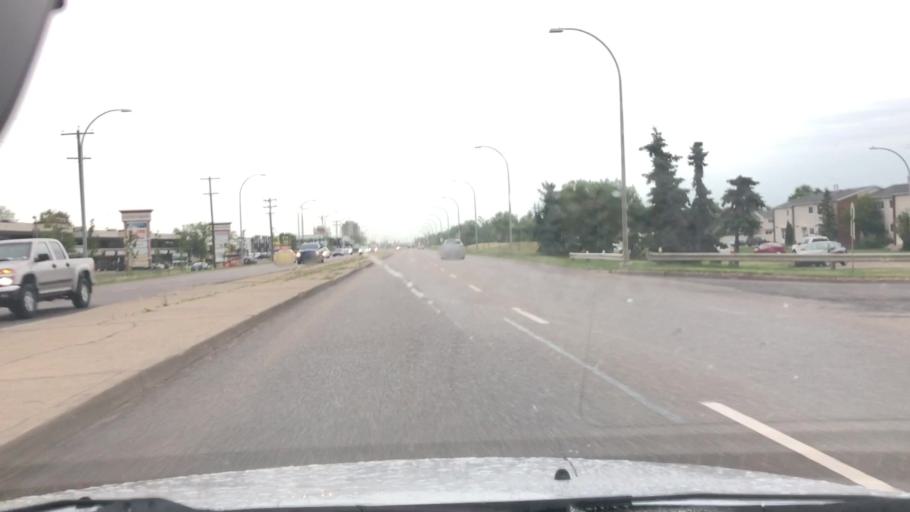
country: CA
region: Alberta
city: St. Albert
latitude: 53.5464
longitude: -113.6128
